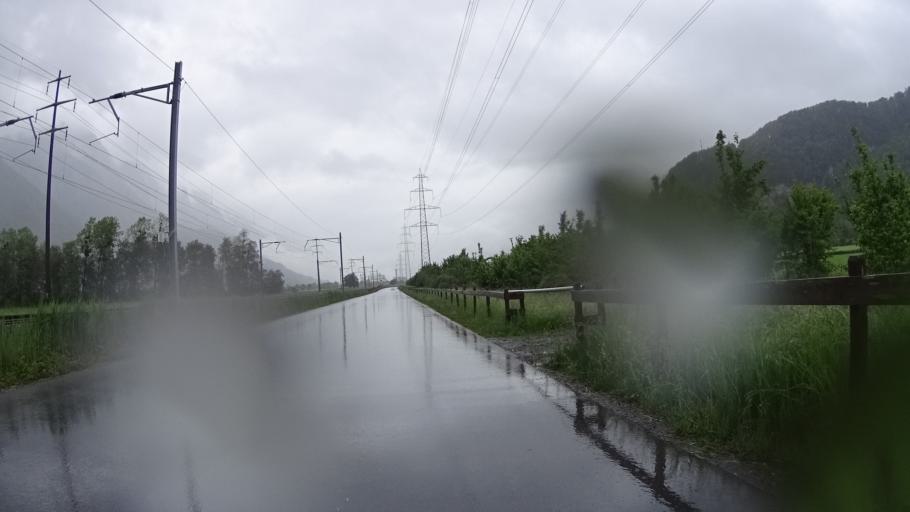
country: CH
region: Saint Gallen
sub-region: Wahlkreis Sarganserland
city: Walenstadt
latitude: 47.1126
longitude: 9.3273
